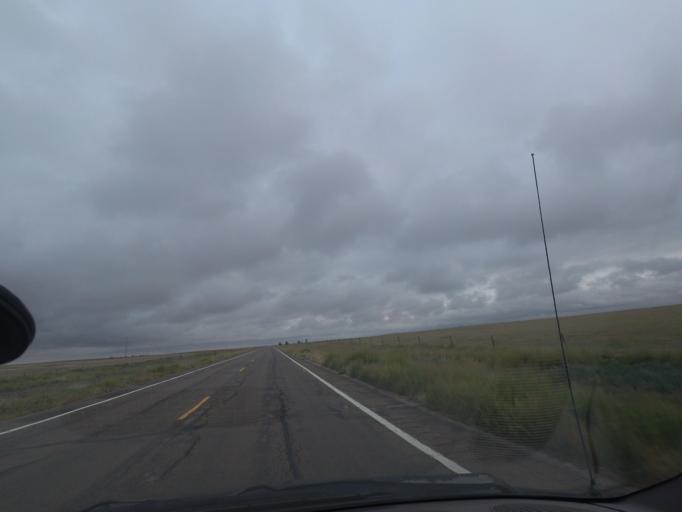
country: US
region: Colorado
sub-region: Yuma County
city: Yuma
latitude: 39.6763
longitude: -102.9604
